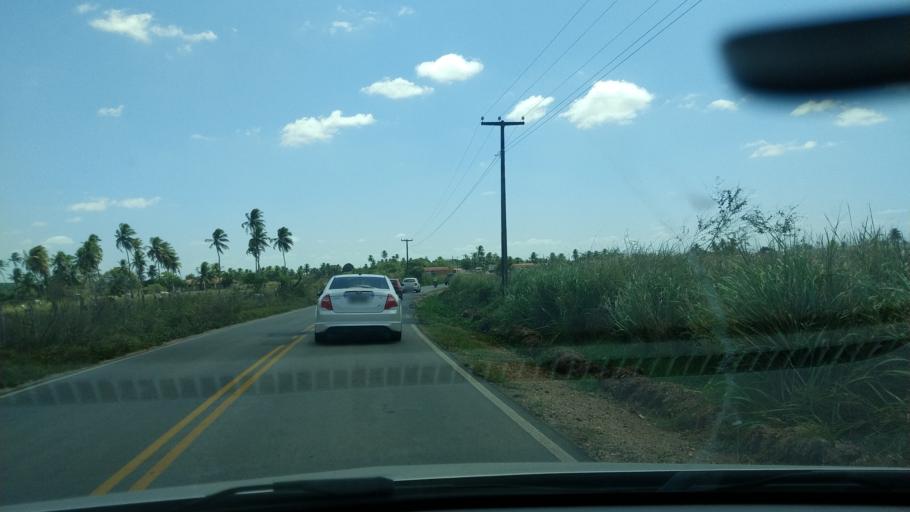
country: BR
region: Rio Grande do Norte
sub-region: Goianinha
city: Goianinha
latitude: -6.2392
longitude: -35.1759
